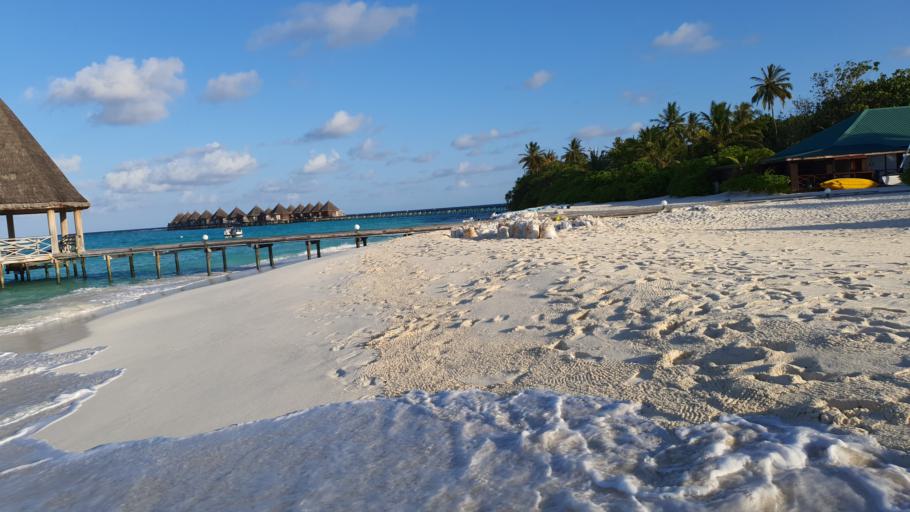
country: MV
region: North Central
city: Mahibadhoo
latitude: 3.6513
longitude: 72.8222
